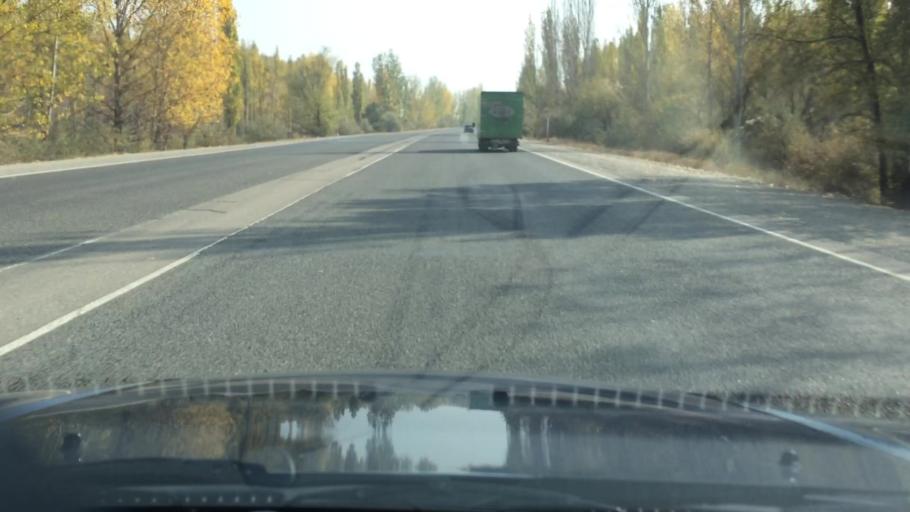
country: KG
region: Chuy
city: Ivanovka
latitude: 42.9379
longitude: 74.9850
